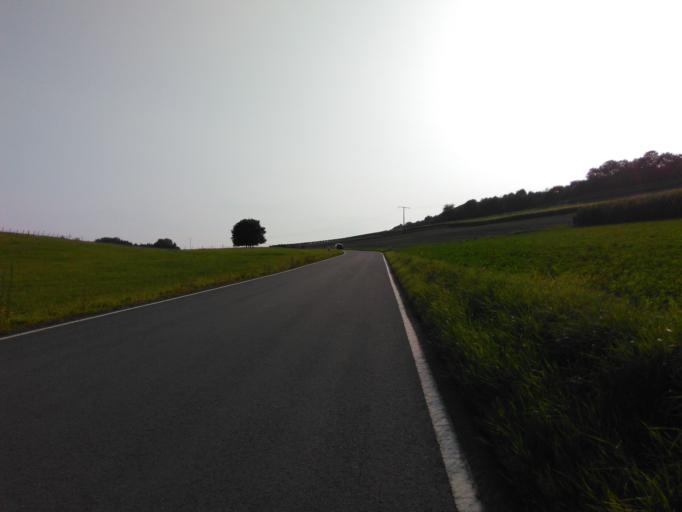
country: DE
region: Rheinland-Pfalz
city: Wellen
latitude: 49.6510
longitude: 6.4234
